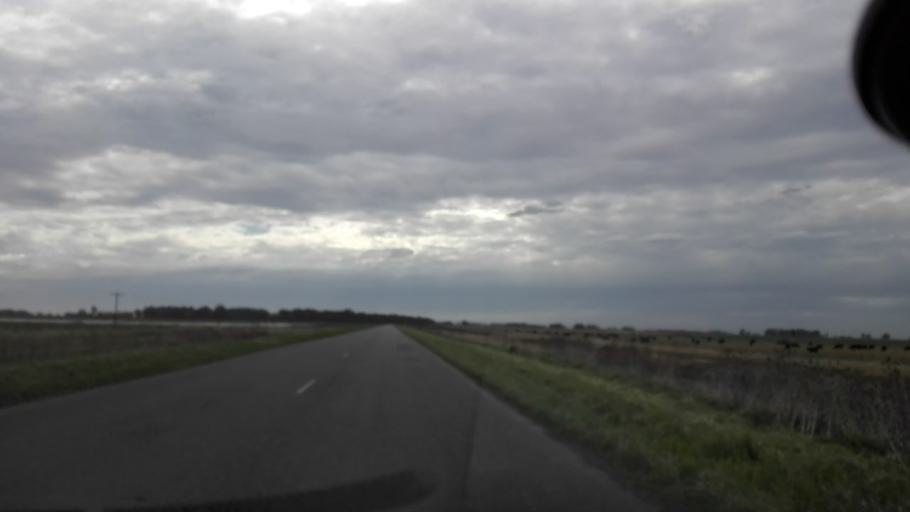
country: AR
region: Buenos Aires
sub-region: Partido de Las Flores
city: Las Flores
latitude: -36.2569
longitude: -59.0473
